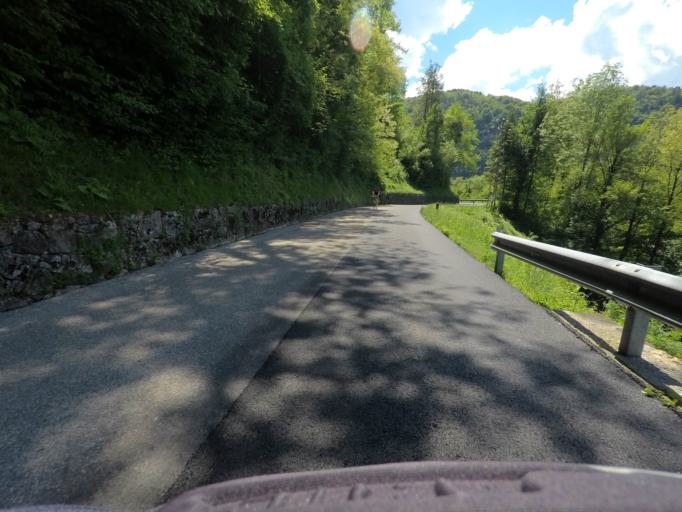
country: IT
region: Friuli Venezia Giulia
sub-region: Provincia di Udine
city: Raveo
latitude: 46.4347
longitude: 12.8878
